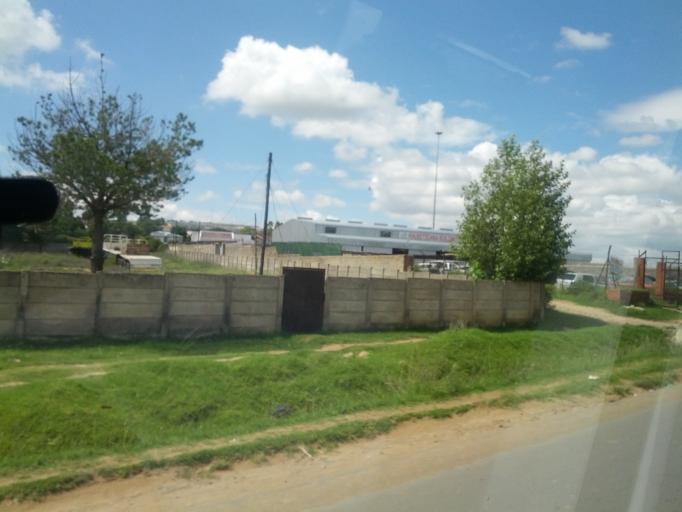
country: LS
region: Maseru
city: Maseru
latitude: -29.2934
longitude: 27.5180
